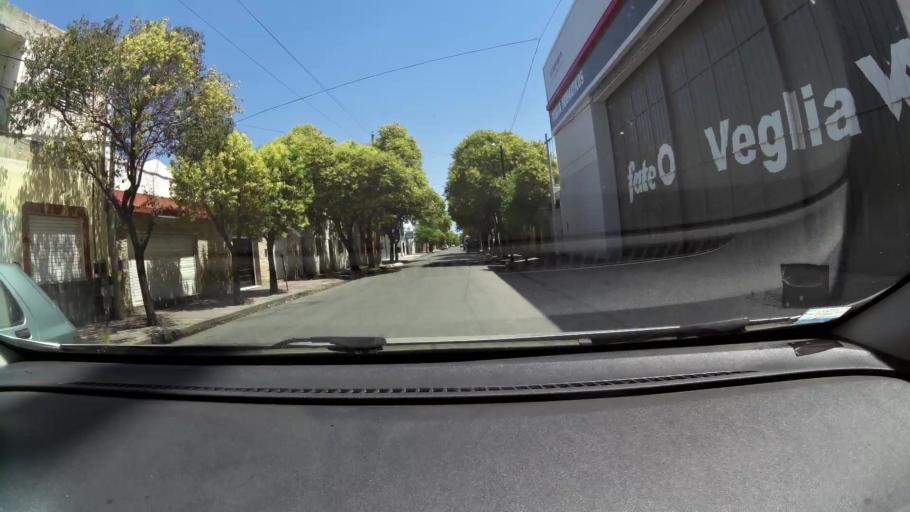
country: AR
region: Cordoba
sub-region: Departamento de Capital
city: Cordoba
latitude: -31.3861
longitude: -64.1582
